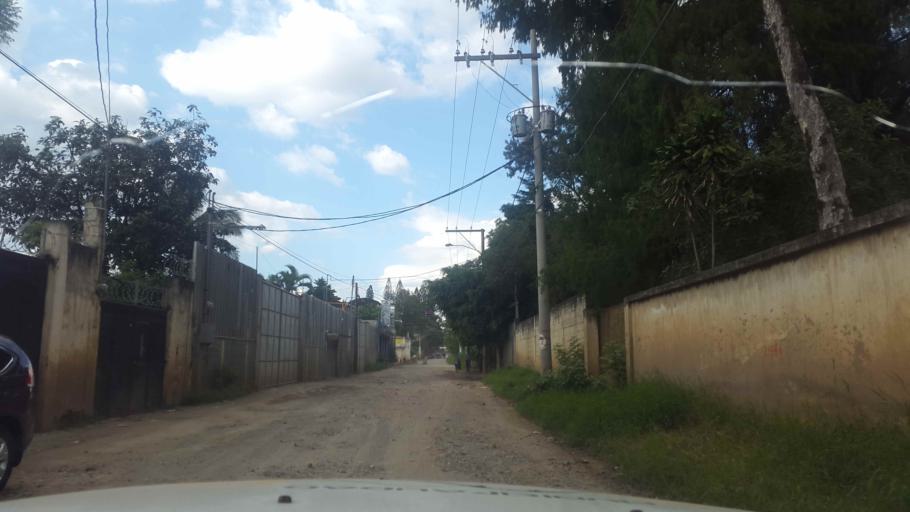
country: GT
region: Guatemala
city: Petapa
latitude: 14.5188
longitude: -90.5365
